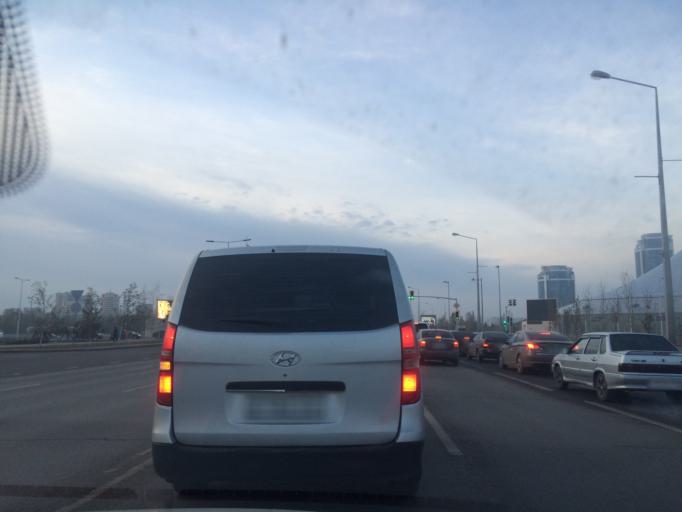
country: KZ
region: Astana Qalasy
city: Astana
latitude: 51.1352
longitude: 71.4079
